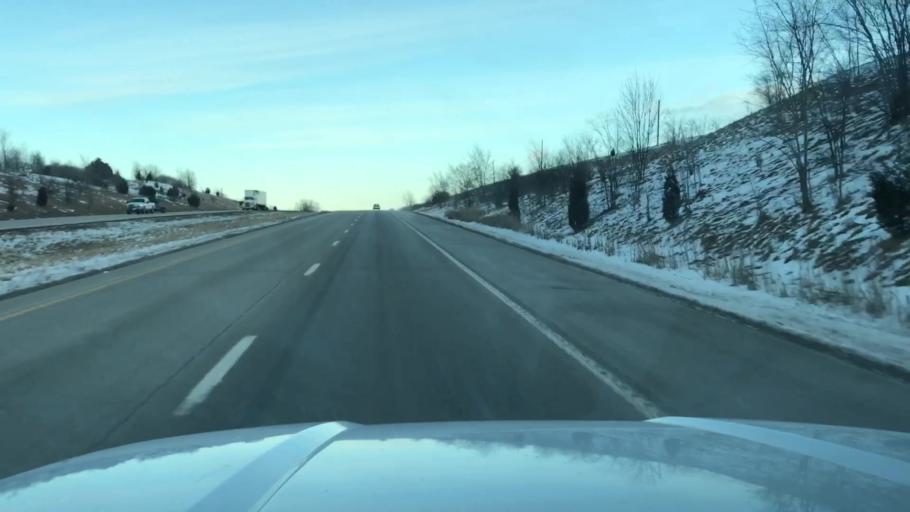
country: US
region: Missouri
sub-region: Buchanan County
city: Saint Joseph
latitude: 39.7476
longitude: -94.7086
